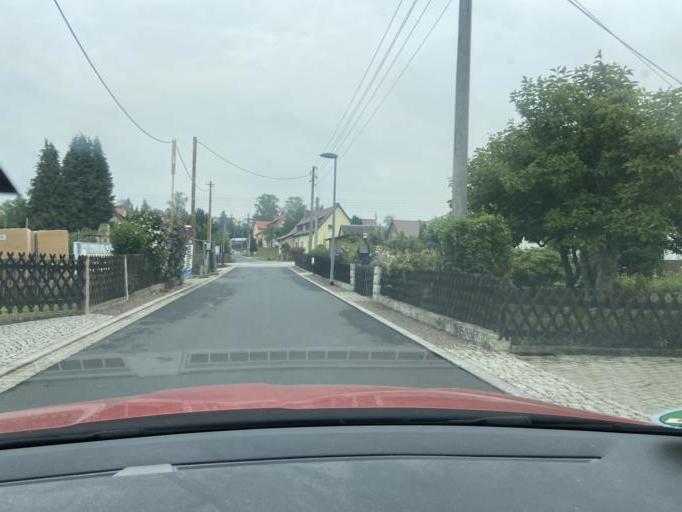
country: DE
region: Saxony
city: Wilsdruff
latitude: 51.0336
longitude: 13.5461
